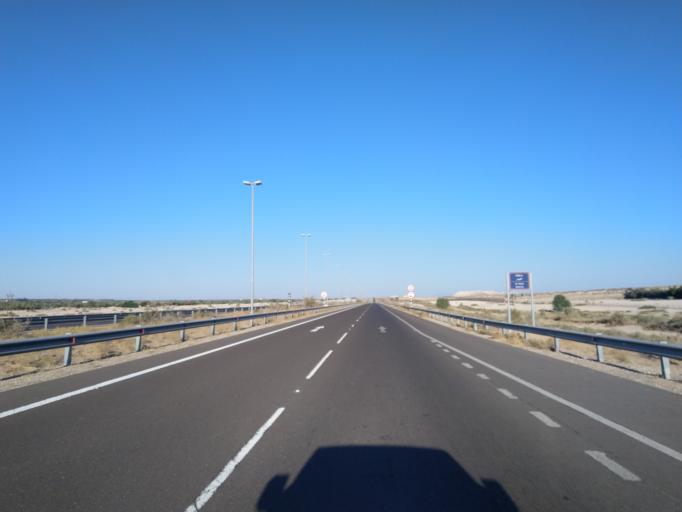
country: OM
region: Al Buraimi
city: Al Buraymi
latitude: 24.5278
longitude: 55.5604
